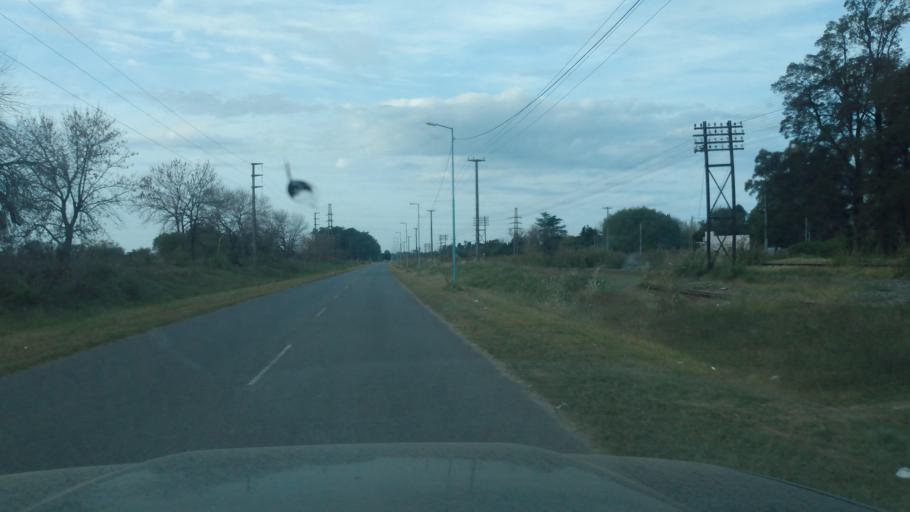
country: AR
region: Buenos Aires
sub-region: Partido de Lujan
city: Lujan
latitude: -34.5901
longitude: -59.1423
